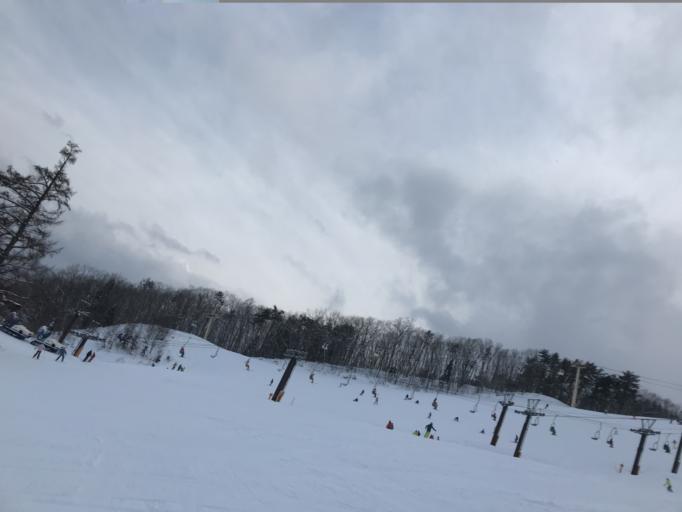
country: JP
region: Nagano
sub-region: Kitaazumi Gun
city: Hakuba
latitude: 36.7031
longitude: 137.8346
